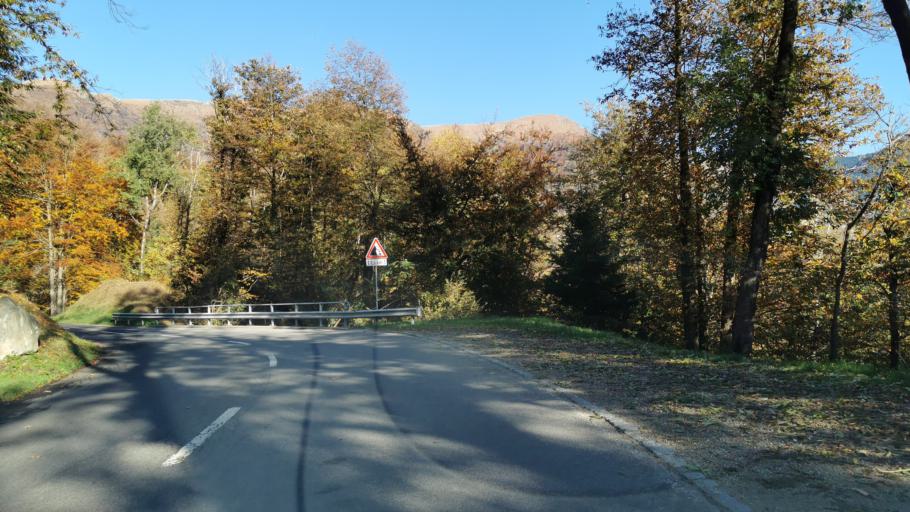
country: CH
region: Ticino
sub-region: Lugano District
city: Pura
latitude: 46.0168
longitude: 8.8550
